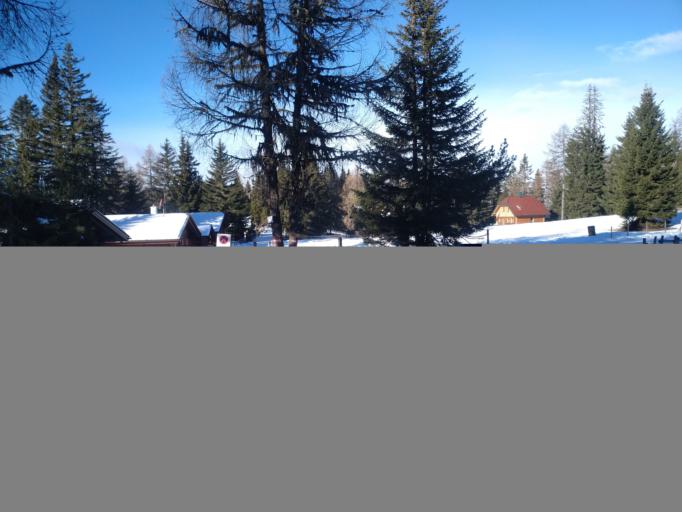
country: AT
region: Carinthia
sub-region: Politischer Bezirk Villach Land
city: Arriach
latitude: 46.6984
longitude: 13.8956
